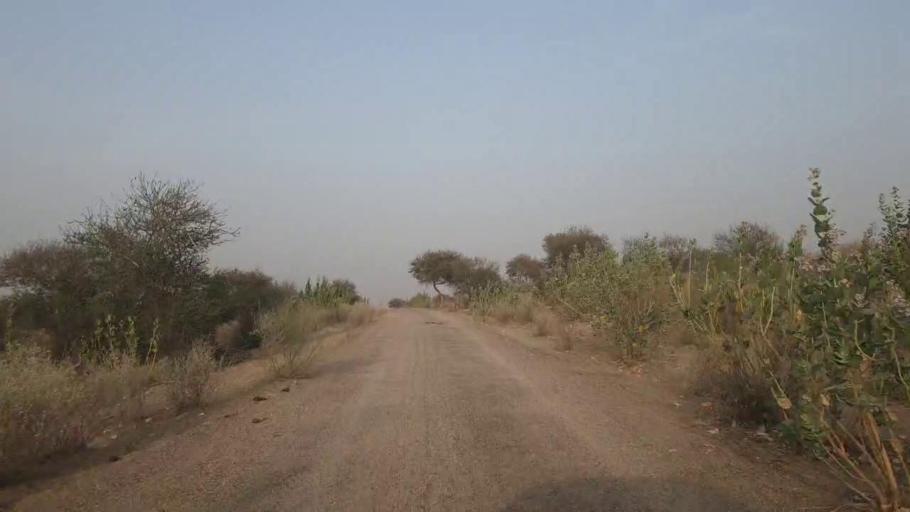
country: PK
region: Sindh
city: Chor
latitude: 25.4934
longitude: 69.9220
